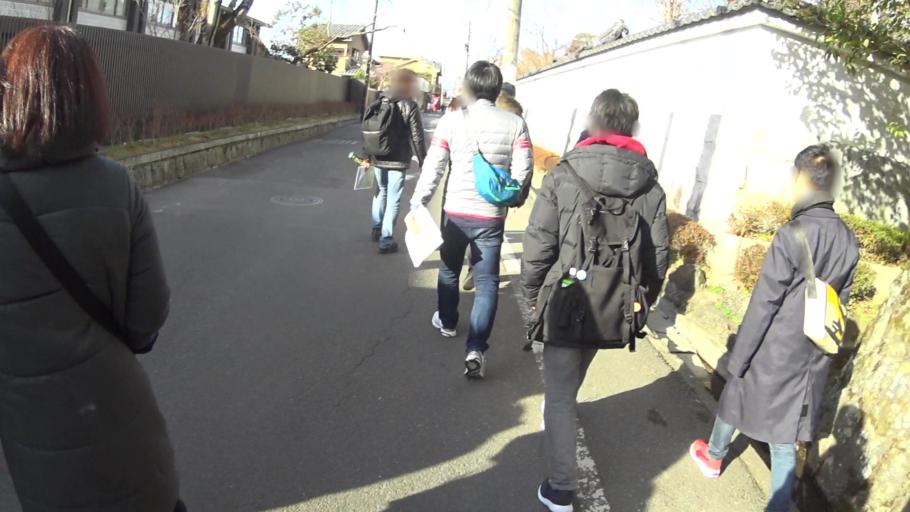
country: JP
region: Kyoto
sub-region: Kyoto-shi
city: Kamigyo-ku
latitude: 35.0136
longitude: 135.7938
